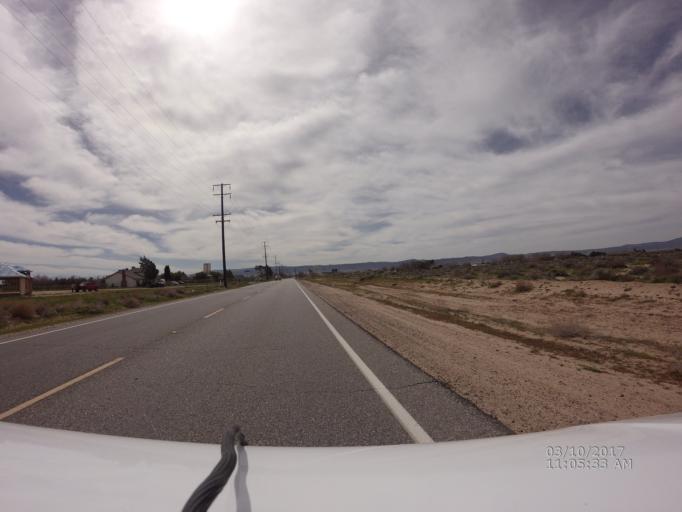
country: US
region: California
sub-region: Los Angeles County
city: Quartz Hill
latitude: 34.7644
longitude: -118.2901
